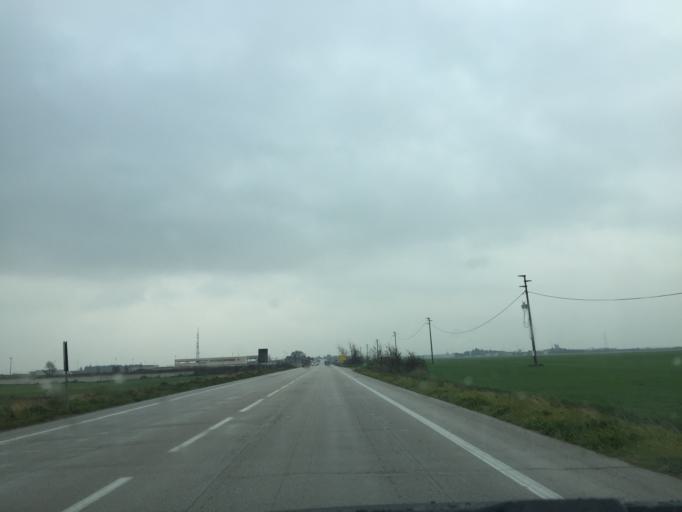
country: IT
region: Apulia
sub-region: Provincia di Foggia
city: Foggia
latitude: 41.4828
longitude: 15.5184
